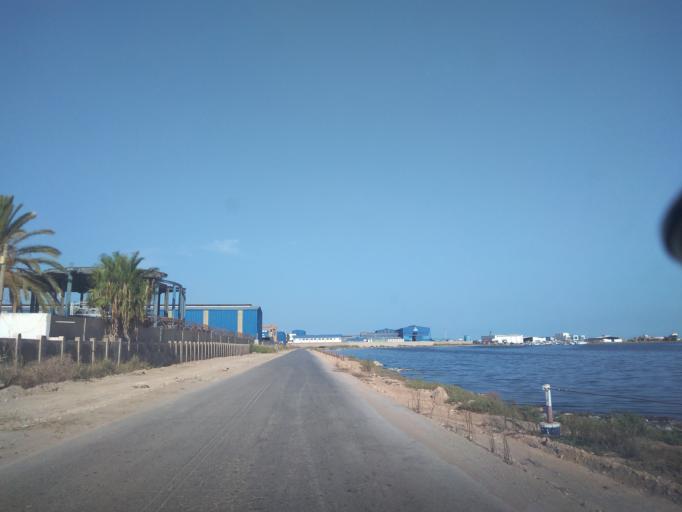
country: TN
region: Safaqis
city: Sfax
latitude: 34.7216
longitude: 10.7617
